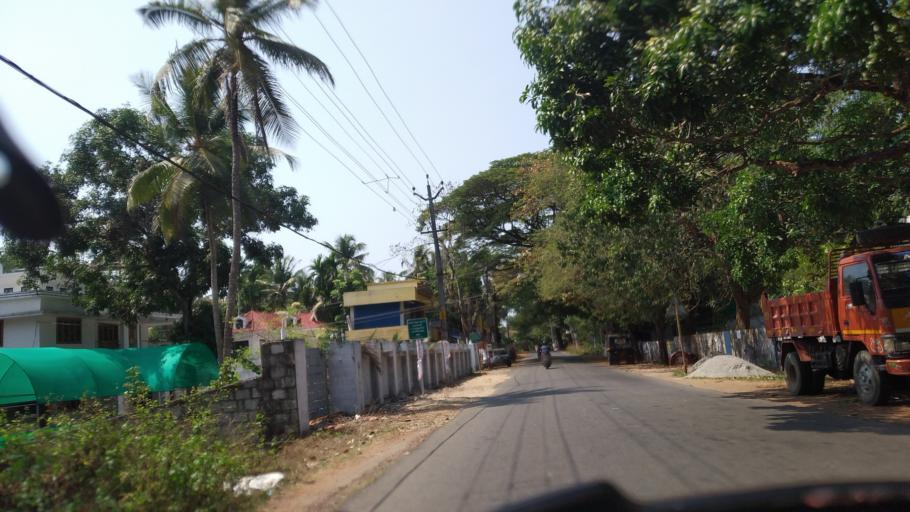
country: IN
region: Kerala
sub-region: Thrissur District
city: Kodungallur
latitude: 10.2399
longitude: 76.1518
